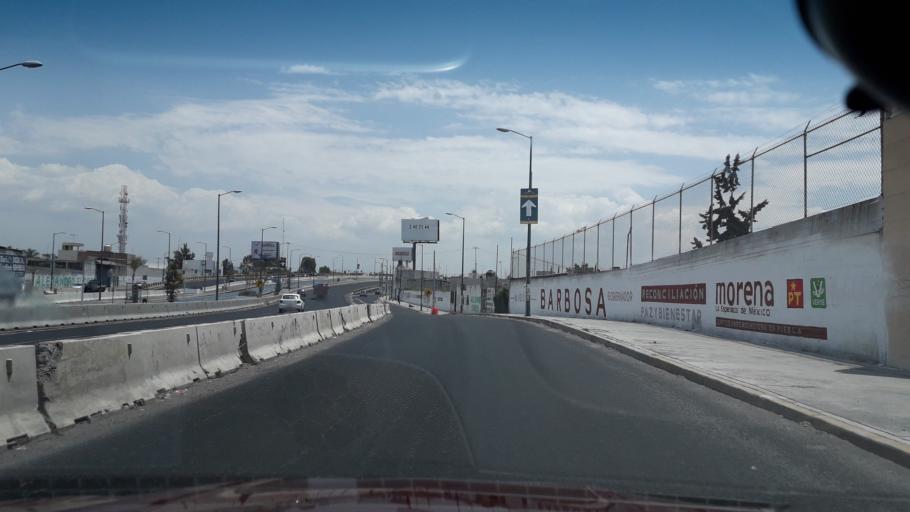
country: MX
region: Puebla
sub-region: Puebla
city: El Capulo (La Quebradora)
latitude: 18.9923
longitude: -98.2489
